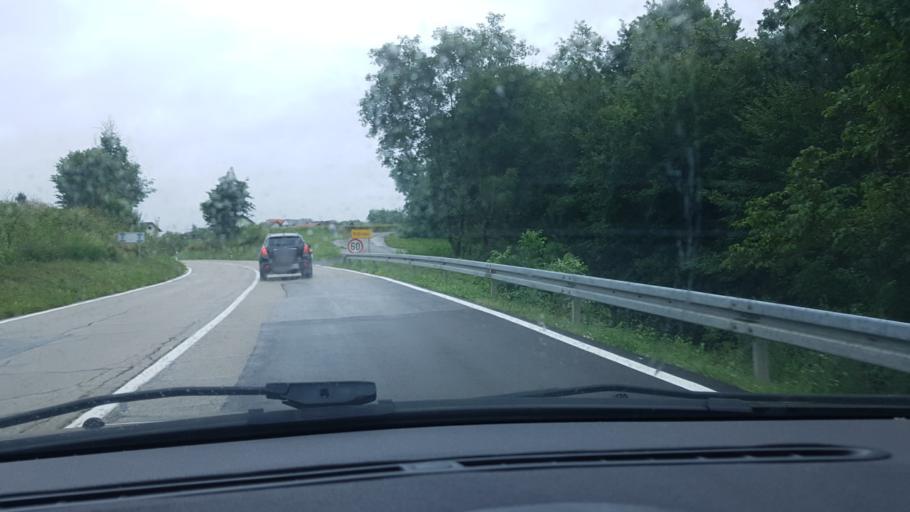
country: HR
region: Karlovacka
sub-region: Grad Karlovac
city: Karlovac
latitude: 45.4540
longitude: 15.4398
